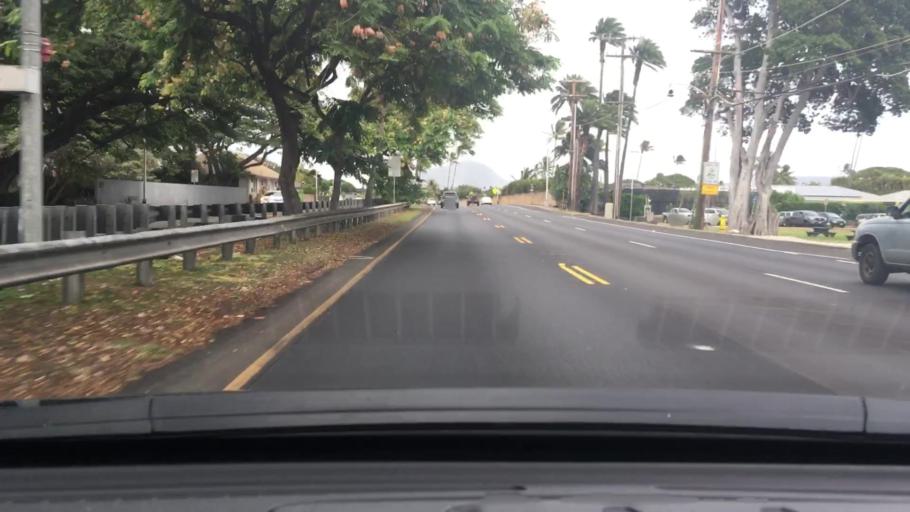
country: US
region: Hawaii
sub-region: Honolulu County
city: Waimanalo
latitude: 21.2765
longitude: -157.7608
